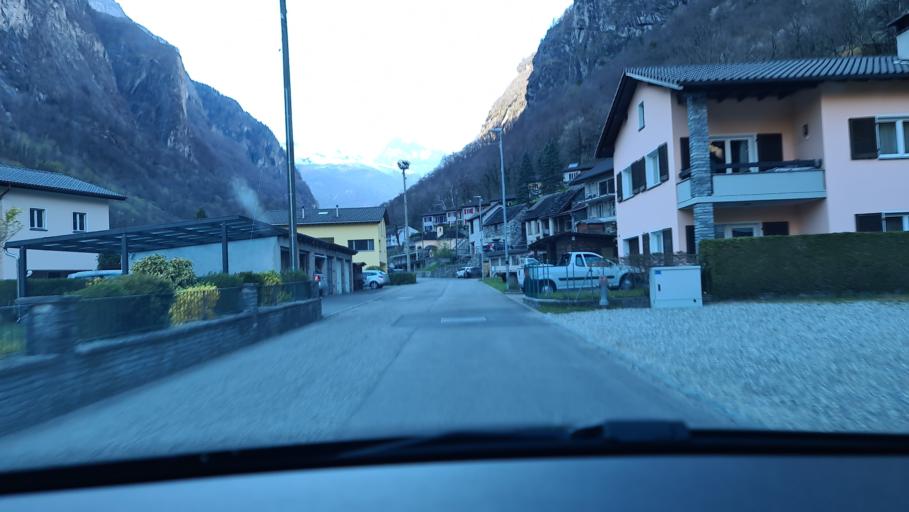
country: CH
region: Ticino
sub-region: Vallemaggia District
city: Cevio
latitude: 46.3458
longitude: 8.6046
